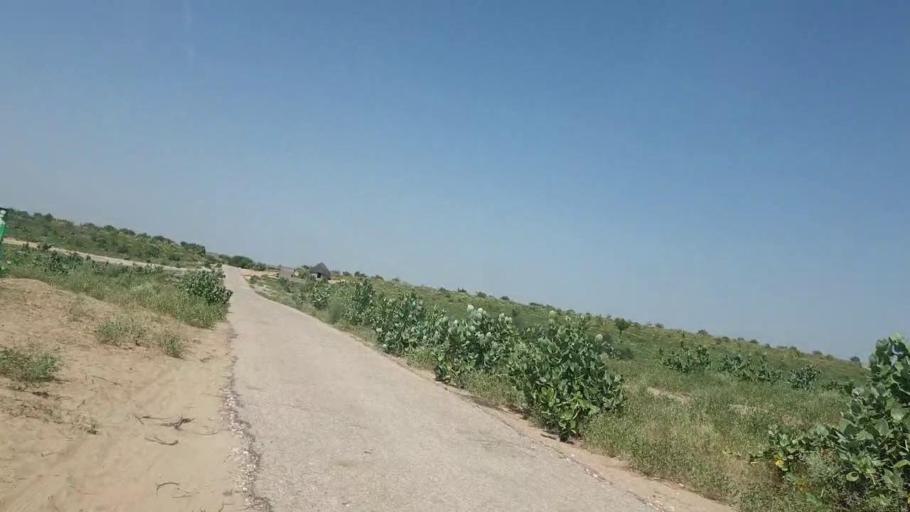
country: PK
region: Sindh
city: Chor
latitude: 25.3609
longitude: 70.3280
